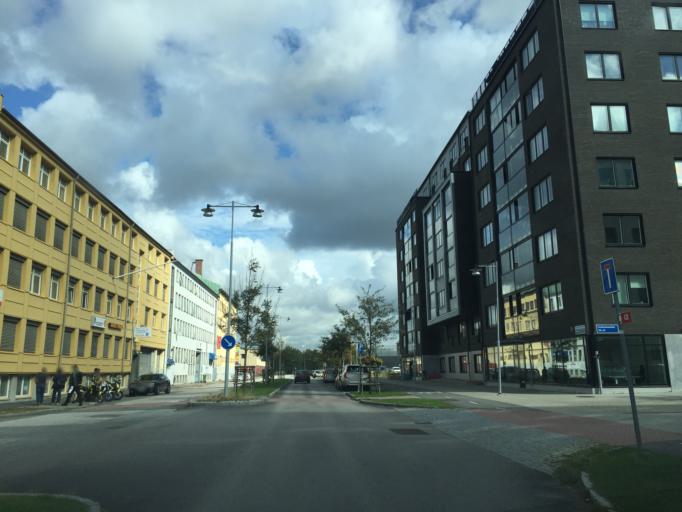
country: SE
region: Vaestra Goetaland
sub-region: Goteborg
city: Majorna
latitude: 57.7087
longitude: 11.9362
